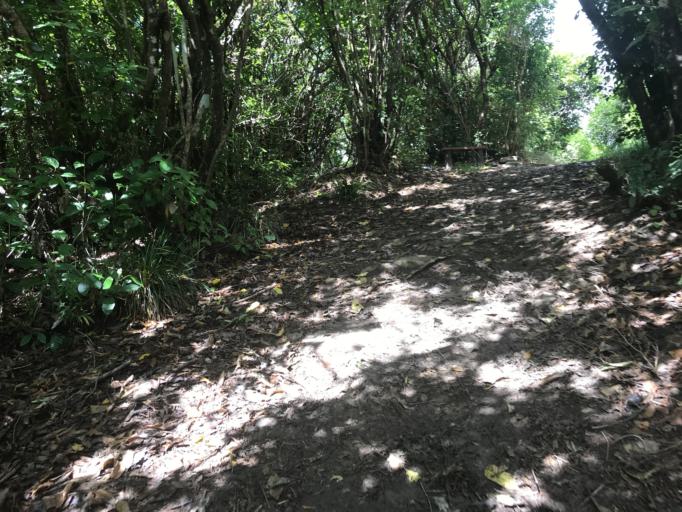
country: NZ
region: Marlborough
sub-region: Marlborough District
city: Picton
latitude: -41.2097
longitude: 174.0198
